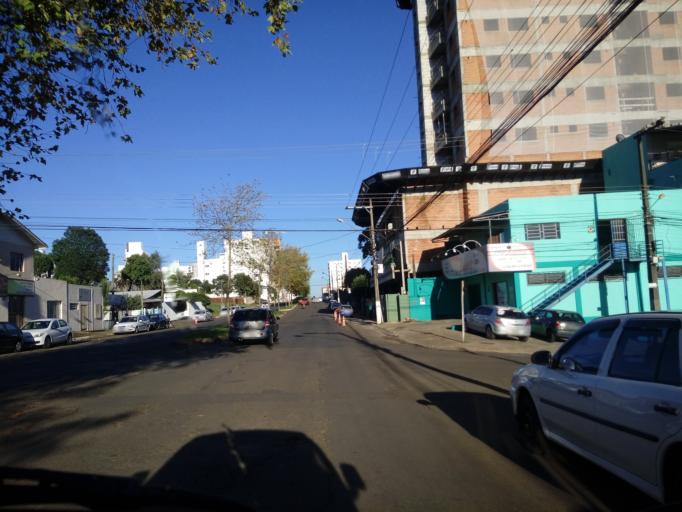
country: BR
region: Santa Catarina
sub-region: Chapeco
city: Chapeco
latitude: -27.0979
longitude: -52.6050
